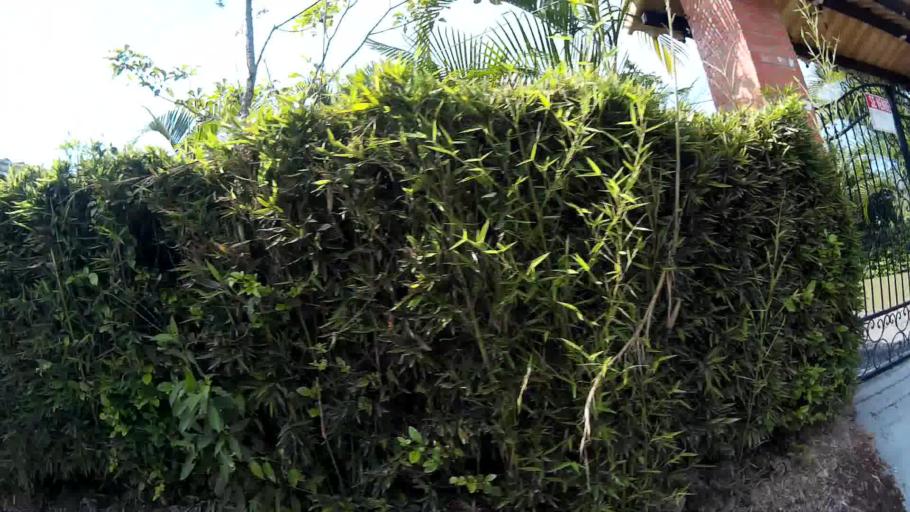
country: CO
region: Valle del Cauca
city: Ulloa
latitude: 4.7079
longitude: -75.6963
